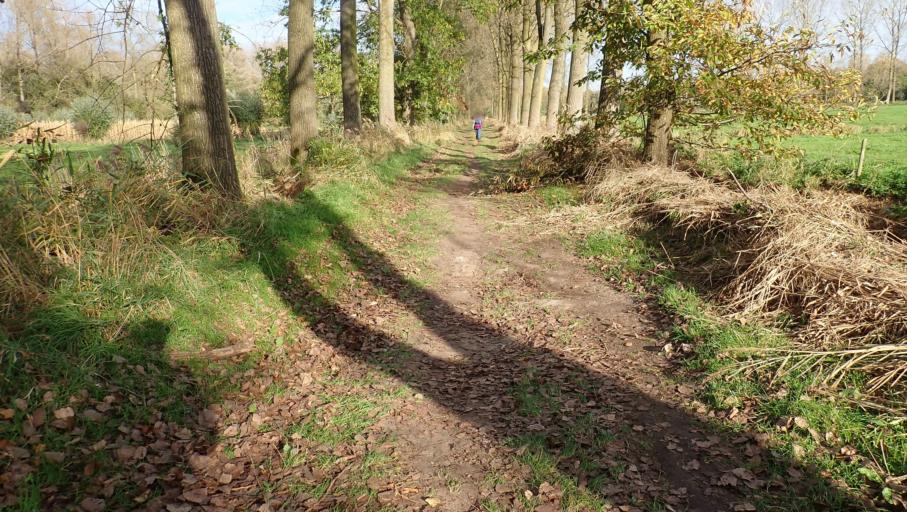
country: BE
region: Flanders
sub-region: Provincie Oost-Vlaanderen
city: Stekene
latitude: 51.1761
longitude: 4.0197
